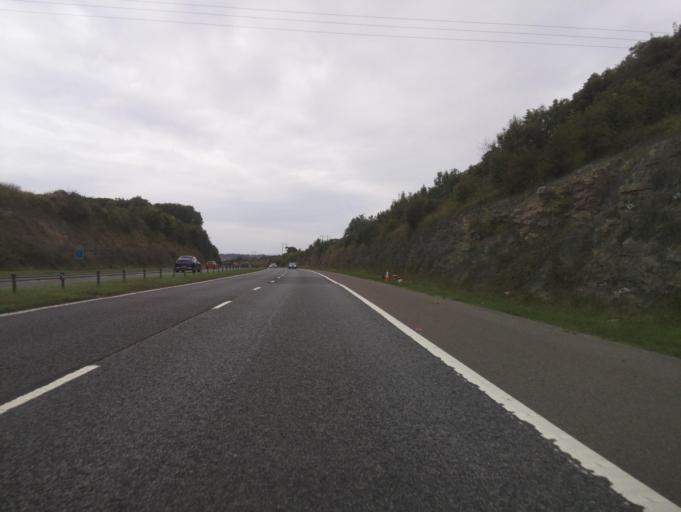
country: GB
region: England
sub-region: County Durham
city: Coxhoe
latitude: 54.6987
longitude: -1.4986
